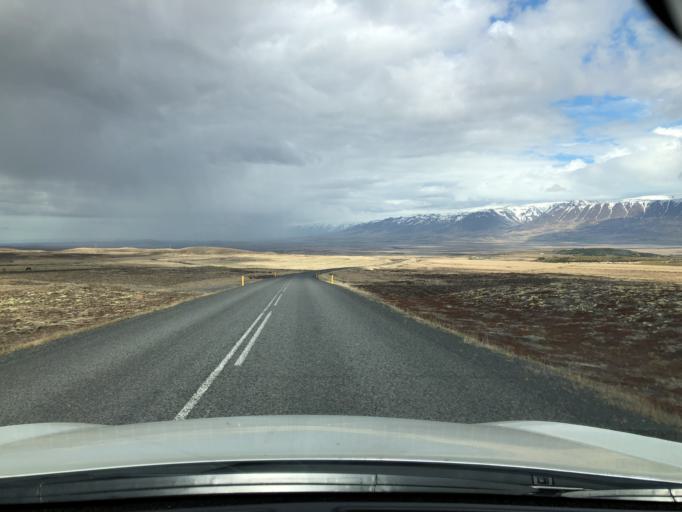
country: IS
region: Northwest
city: Saudarkrokur
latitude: 65.5337
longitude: -19.5119
